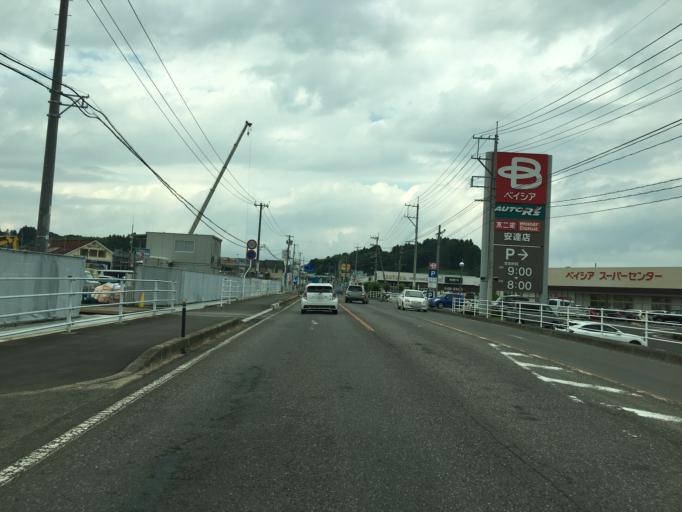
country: JP
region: Fukushima
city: Nihommatsu
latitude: 37.6126
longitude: 140.4615
